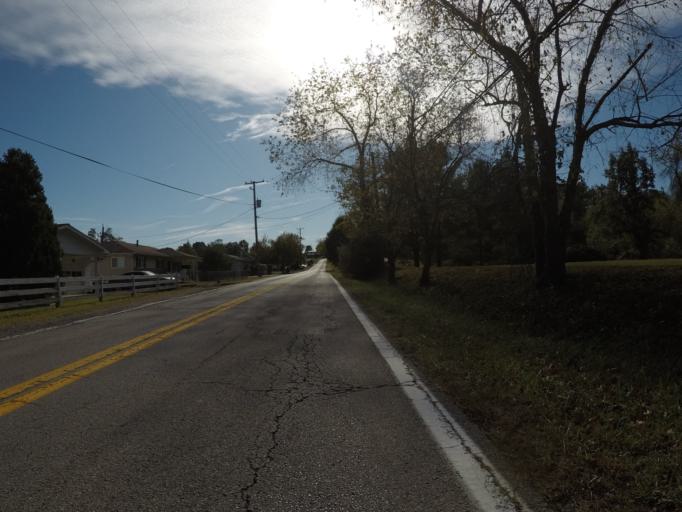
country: US
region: Ohio
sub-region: Lawrence County
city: Burlington
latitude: 38.3607
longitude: -82.5278
